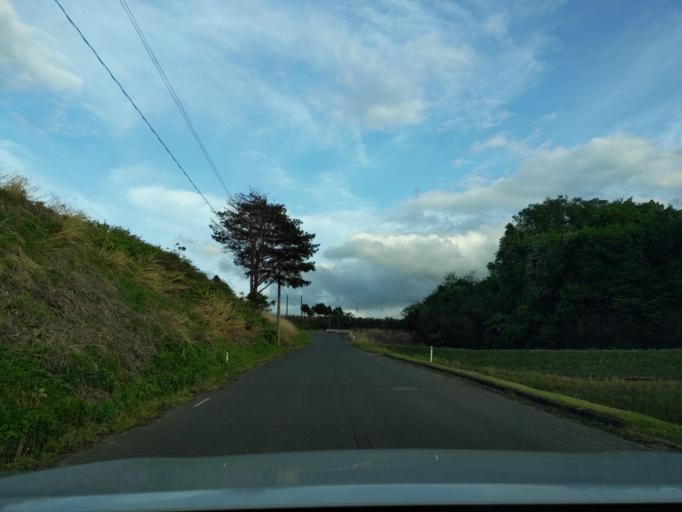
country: JP
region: Fukushima
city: Miharu
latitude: 37.4127
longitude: 140.4684
